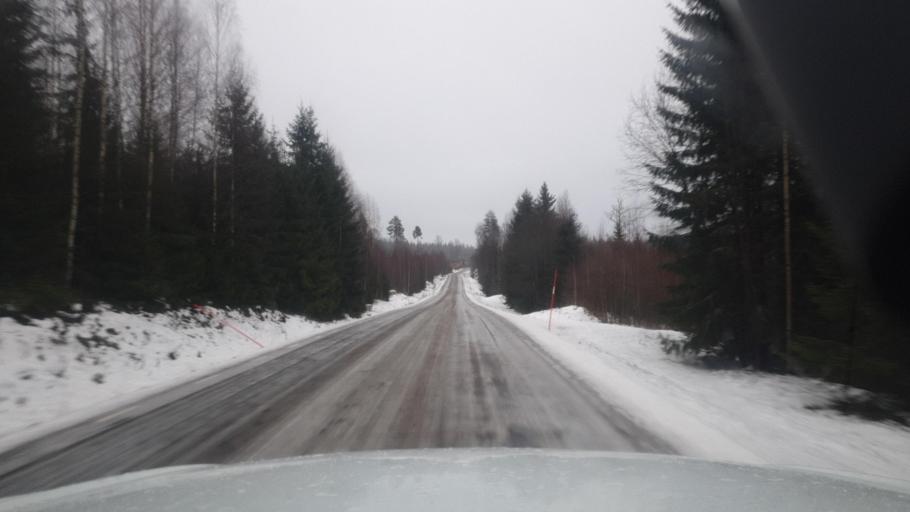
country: SE
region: Vaermland
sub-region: Torsby Kommun
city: Torsby
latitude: 59.9911
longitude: 12.7466
